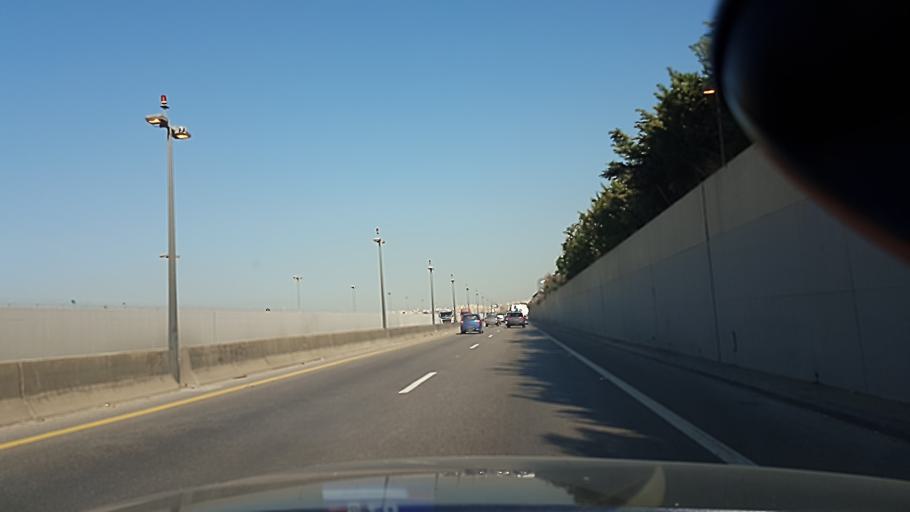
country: LB
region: Mont-Liban
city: Baabda
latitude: 33.8143
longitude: 35.4957
